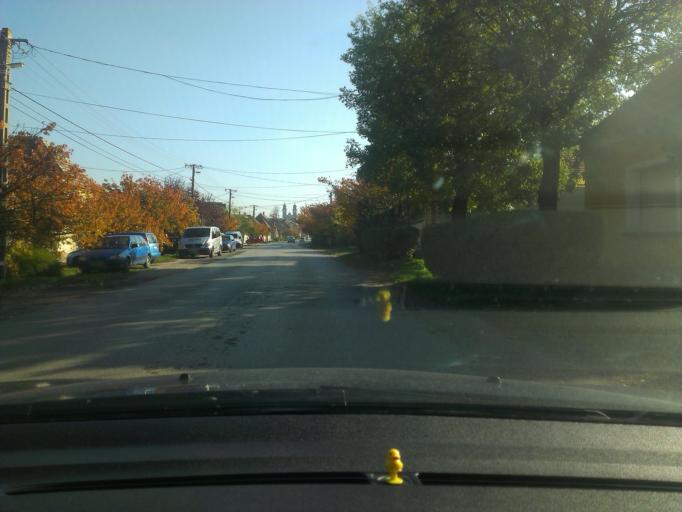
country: HU
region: Komarom-Esztergom
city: Tata
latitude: 47.6480
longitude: 18.3033
